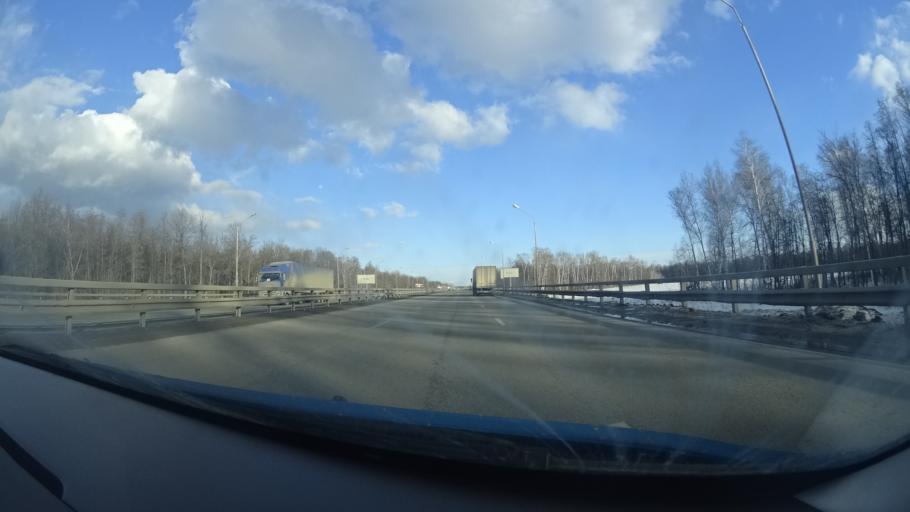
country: RU
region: Bashkortostan
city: Avdon
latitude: 54.6696
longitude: 55.8410
